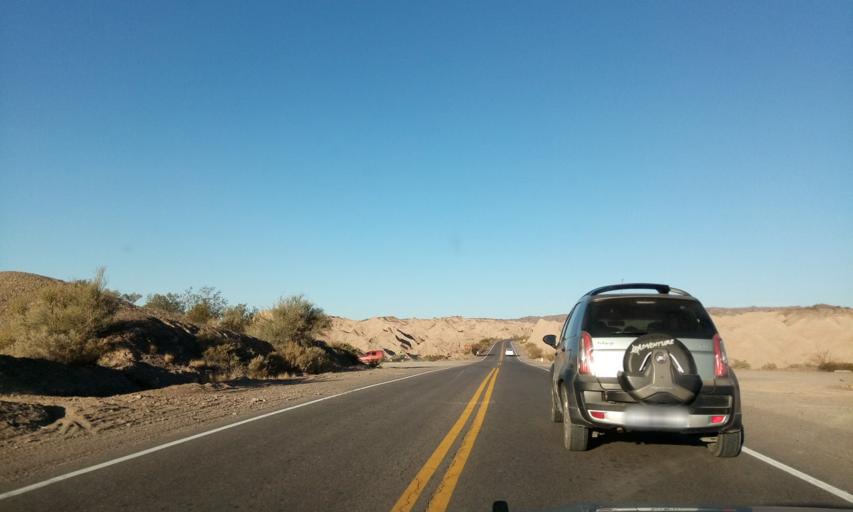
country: AR
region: San Juan
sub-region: Departamento de Rivadavia
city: Rivadavia
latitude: -31.4461
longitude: -68.6492
